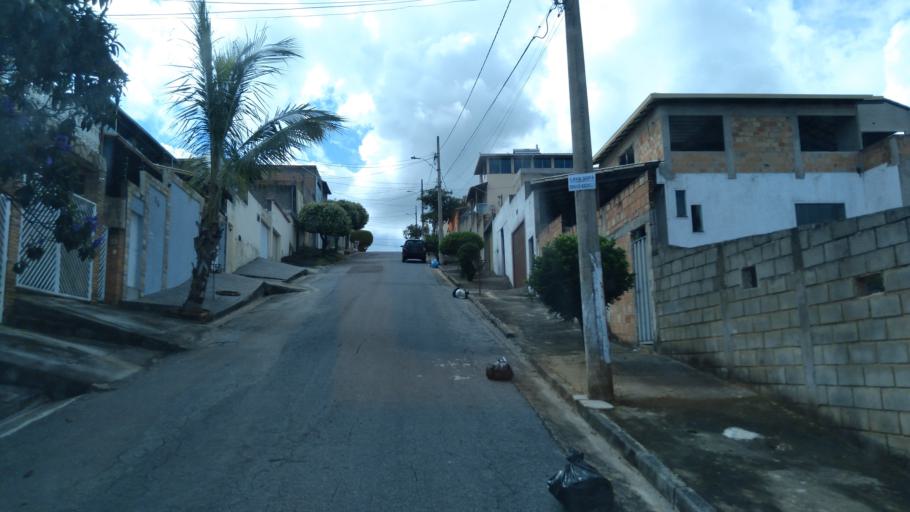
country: BR
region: Minas Gerais
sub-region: Belo Horizonte
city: Belo Horizonte
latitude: -19.8614
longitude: -43.8856
